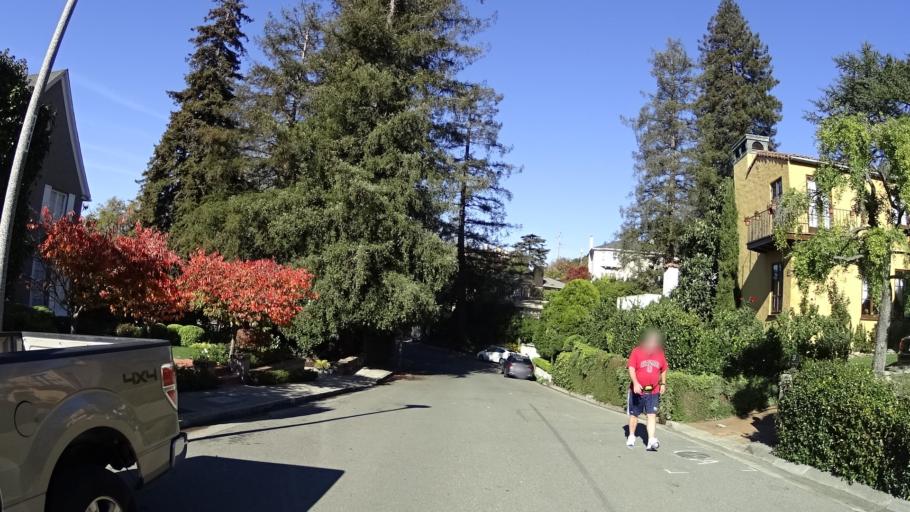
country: US
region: California
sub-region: Alameda County
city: Piedmont
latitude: 37.8216
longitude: -122.2304
